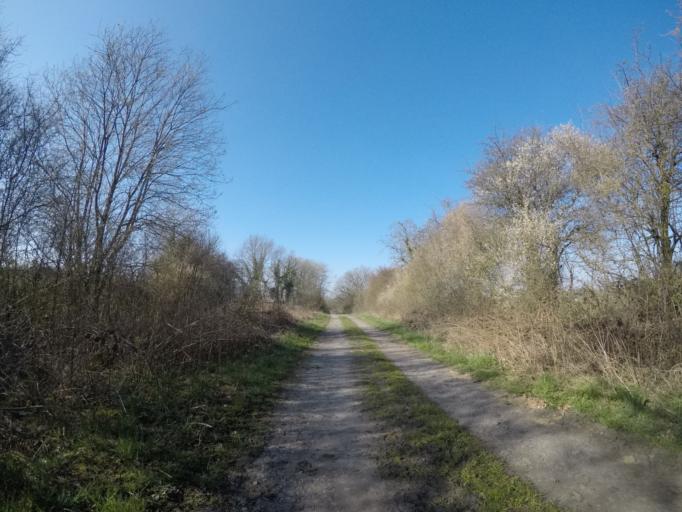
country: BE
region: Wallonia
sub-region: Province du Luxembourg
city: Habay-la-Vieille
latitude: 49.7049
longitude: 5.5972
